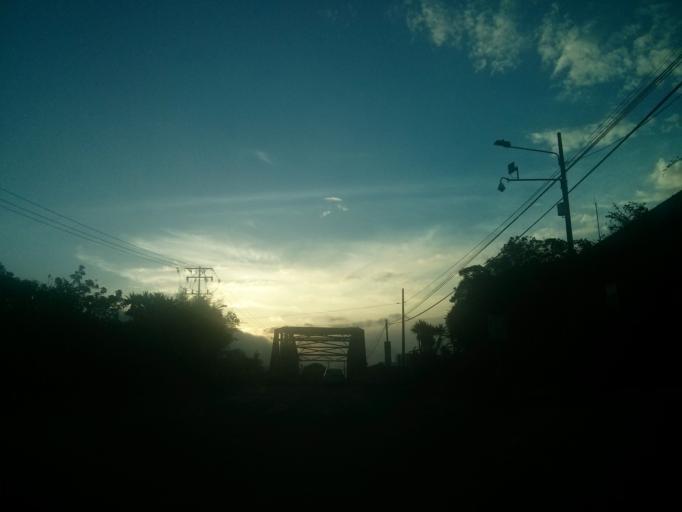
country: CR
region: Cartago
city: Cartago
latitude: 9.8808
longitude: -83.9195
